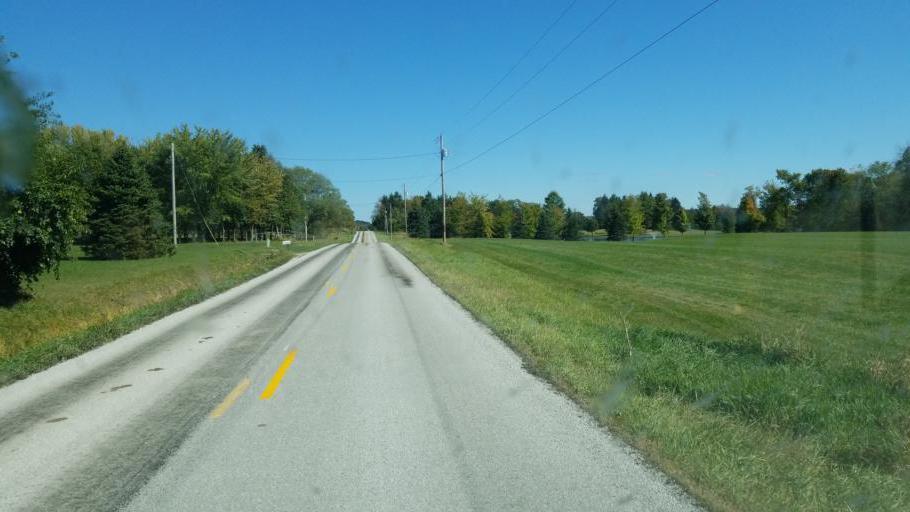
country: US
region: Ohio
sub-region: Ashland County
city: Ashland
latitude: 40.9928
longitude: -82.2711
